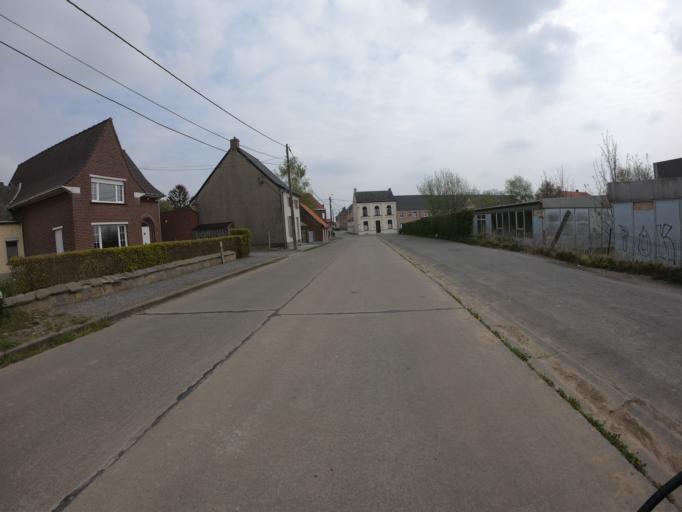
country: BE
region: Wallonia
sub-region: Province du Hainaut
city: Celles
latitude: 50.7468
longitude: 3.5054
